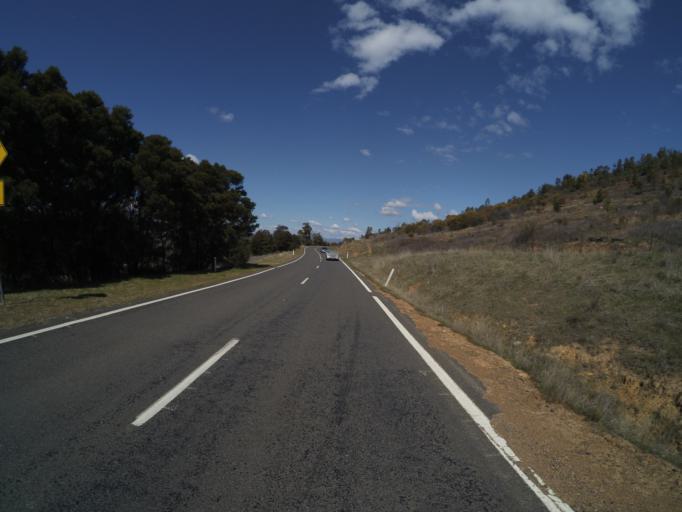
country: AU
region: Australian Capital Territory
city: Macquarie
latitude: -35.3056
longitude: 148.9479
